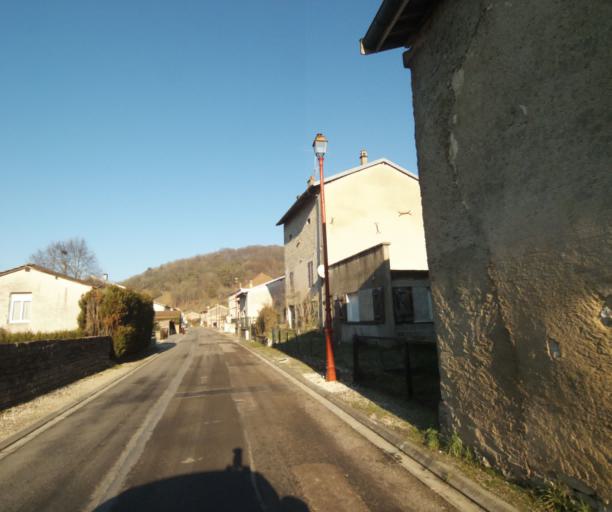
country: FR
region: Champagne-Ardenne
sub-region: Departement de la Haute-Marne
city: Chevillon
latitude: 48.4956
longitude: 5.1918
